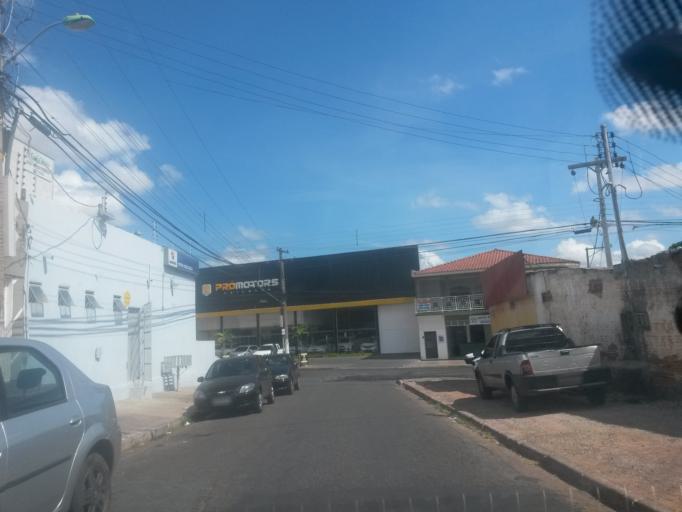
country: BR
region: Mato Grosso
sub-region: Cuiaba
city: Cuiaba
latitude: -15.6123
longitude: -56.0837
